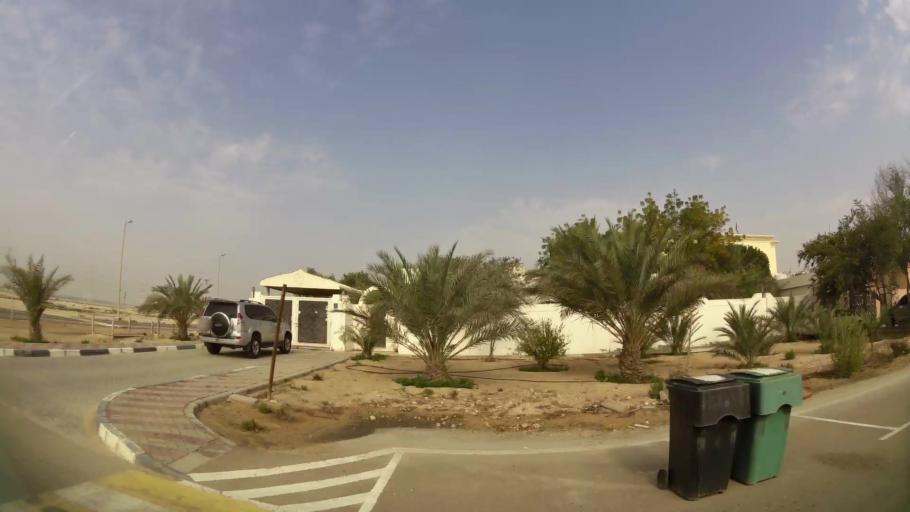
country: AE
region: Abu Dhabi
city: Abu Dhabi
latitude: 24.6541
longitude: 54.7643
